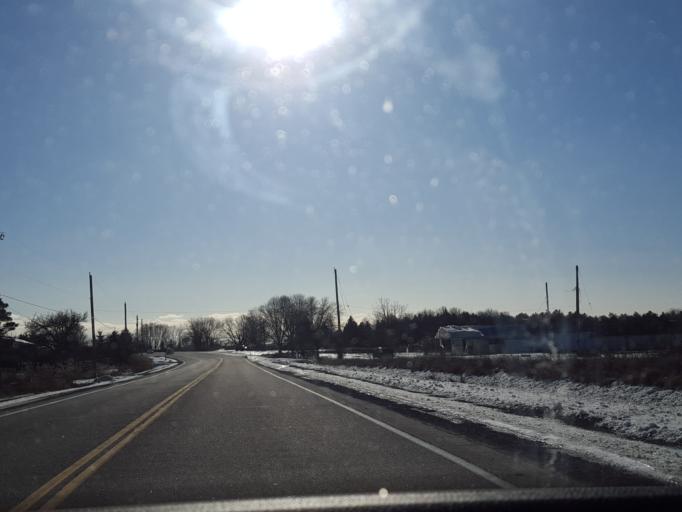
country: CA
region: Ontario
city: Oshawa
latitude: 43.9827
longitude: -78.9621
